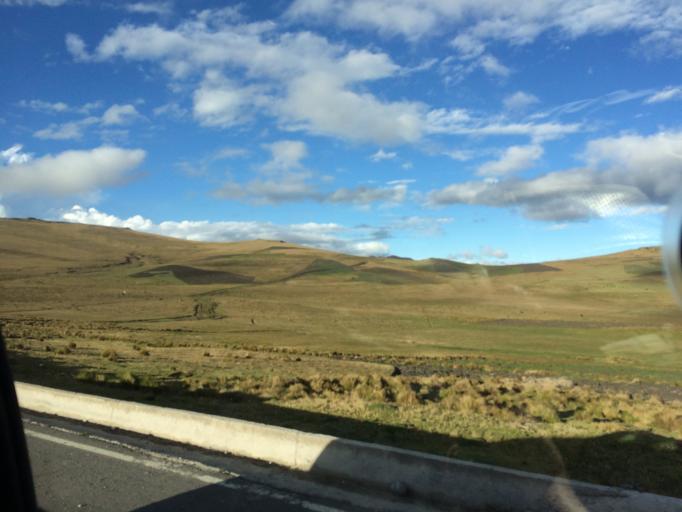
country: EC
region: Chimborazo
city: Alausi
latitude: -2.2336
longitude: -78.6834
